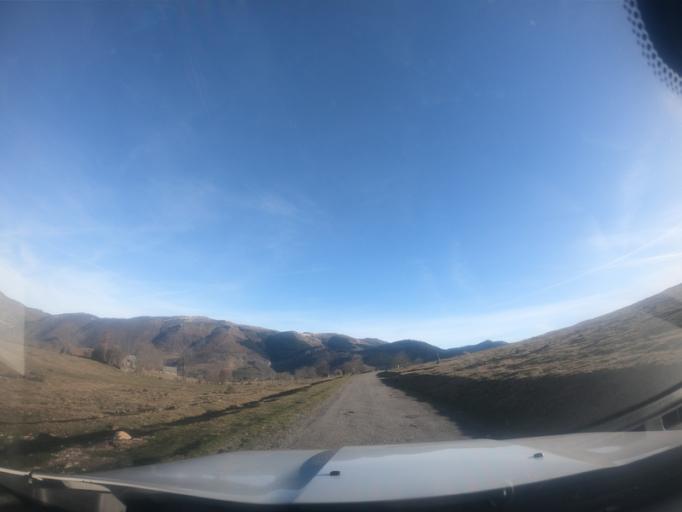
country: FR
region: Midi-Pyrenees
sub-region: Departement des Hautes-Pyrenees
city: Campan
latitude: 42.9459
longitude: 0.2371
